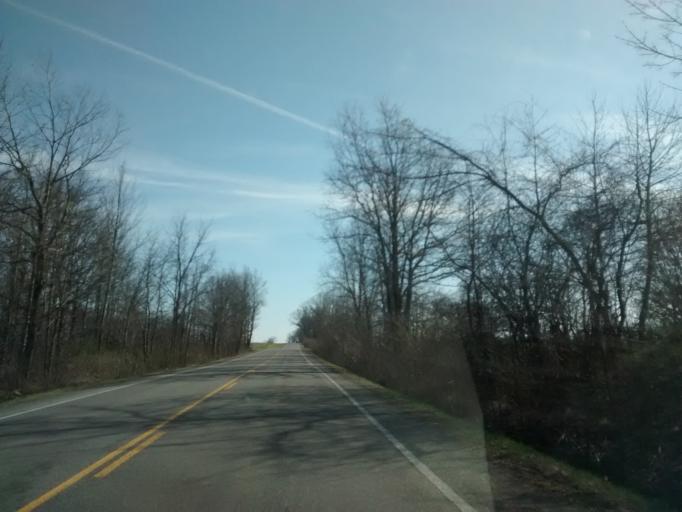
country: US
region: New York
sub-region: Livingston County
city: Avon
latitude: 42.9610
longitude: -77.7635
